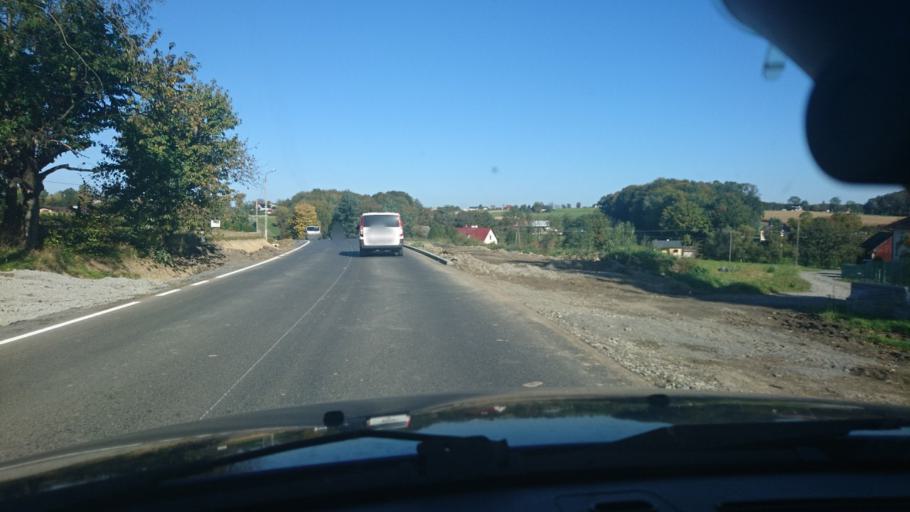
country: PL
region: Silesian Voivodeship
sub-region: Powiat bielski
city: Bronow
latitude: 49.8489
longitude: 18.9013
